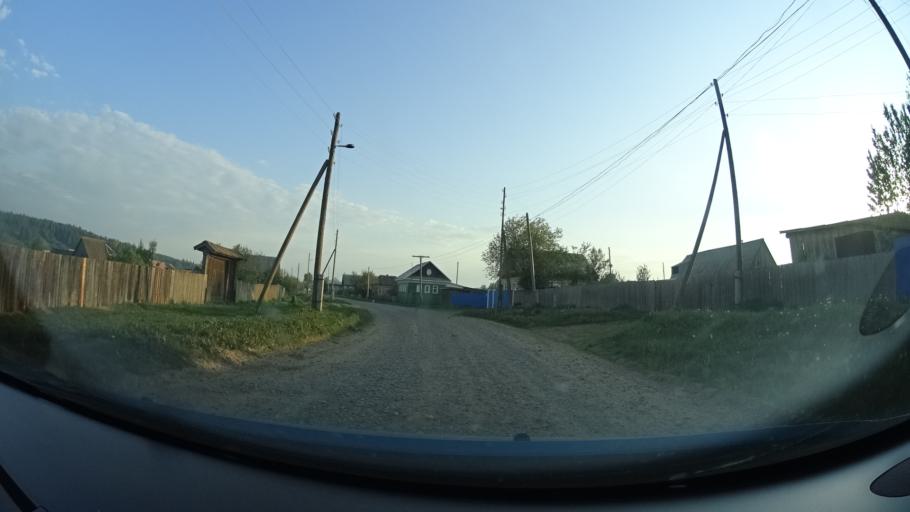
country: RU
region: Perm
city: Kuyeda
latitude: 56.6699
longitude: 55.6933
